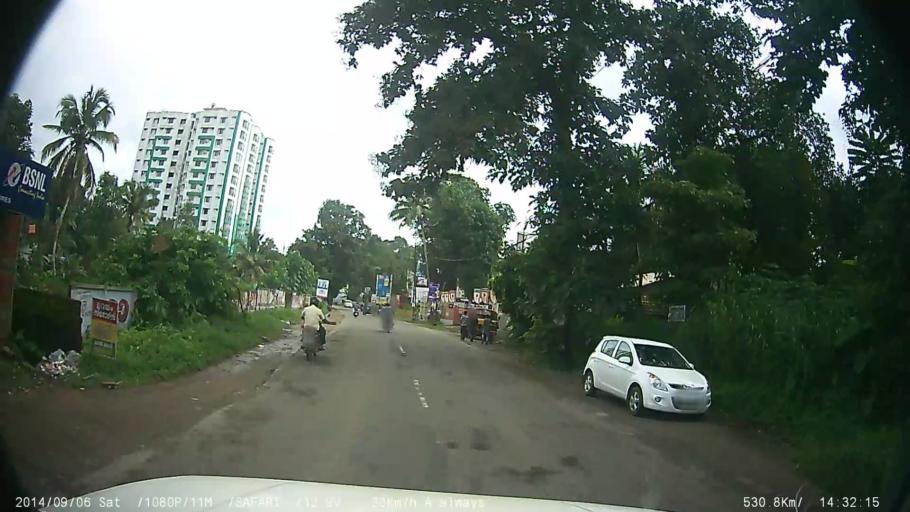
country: IN
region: Kerala
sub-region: Kottayam
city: Kottayam
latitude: 9.6153
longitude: 76.5323
